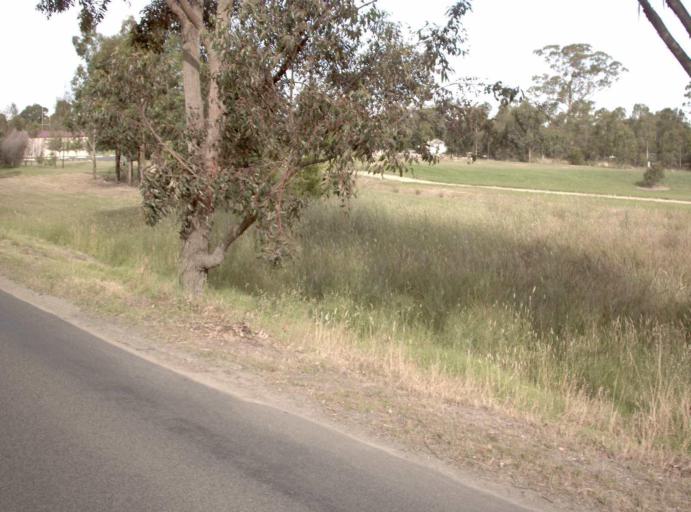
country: AU
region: Victoria
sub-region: Latrobe
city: Traralgon
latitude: -38.0621
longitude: 146.6216
